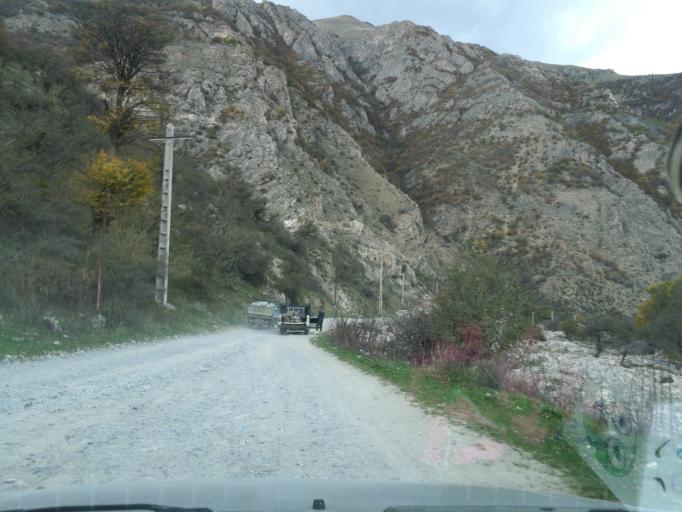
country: IR
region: Mazandaran
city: `Abbasabad
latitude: 36.4447
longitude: 51.0632
